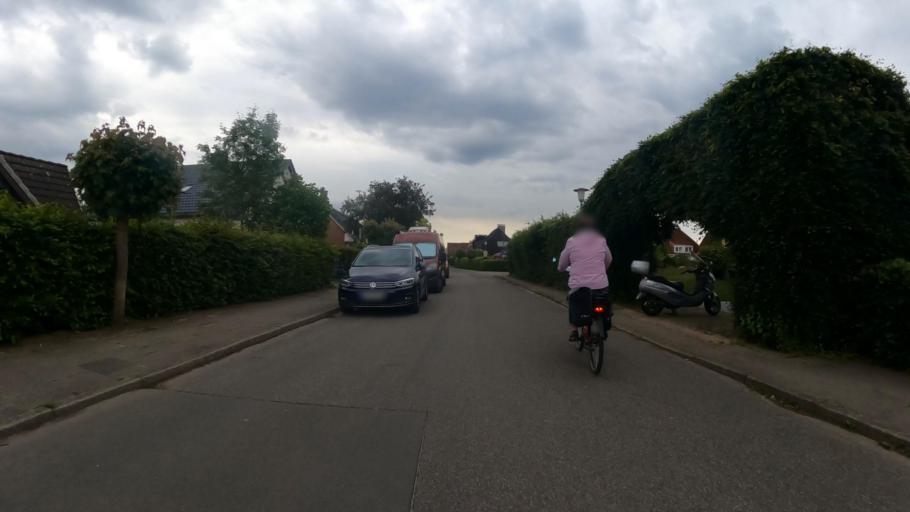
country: DE
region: Schleswig-Holstein
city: Rellingen
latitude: 53.6450
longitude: 9.8186
